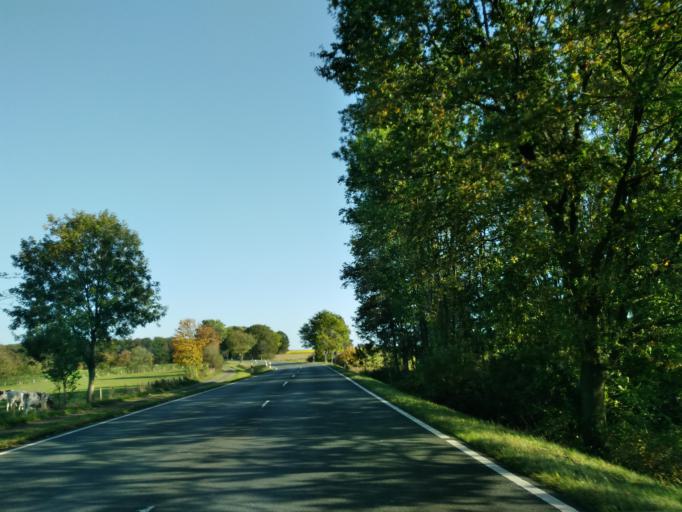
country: DE
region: Rheinland-Pfalz
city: Kircheib
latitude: 50.7082
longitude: 7.4241
